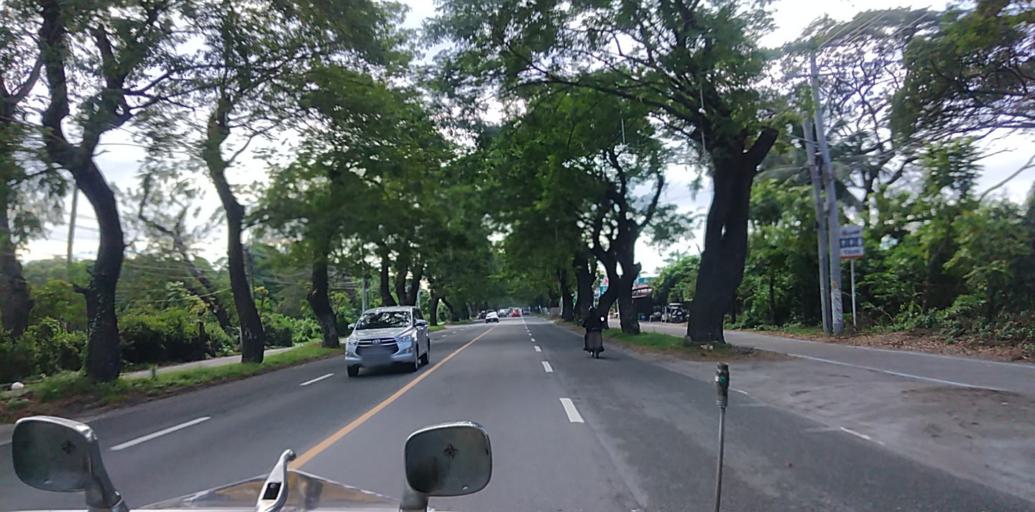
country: PH
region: Central Luzon
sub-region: Province of Pampanga
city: Telabastagan
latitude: 15.1073
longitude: 120.6150
